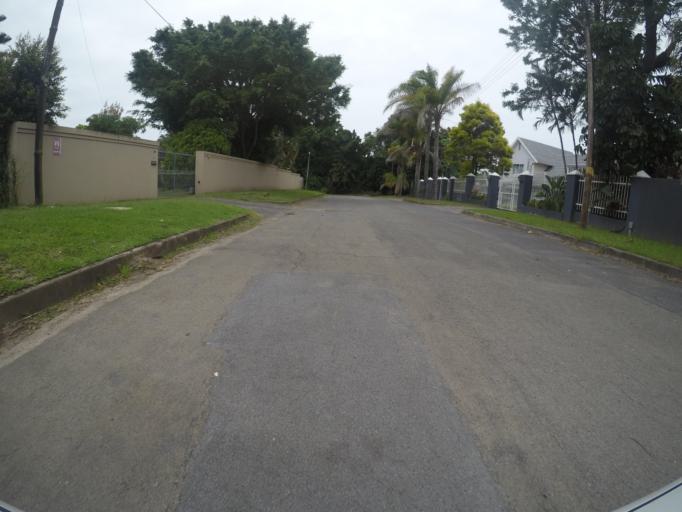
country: ZA
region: Eastern Cape
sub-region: Buffalo City Metropolitan Municipality
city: East London
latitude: -32.9745
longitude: 27.9296
